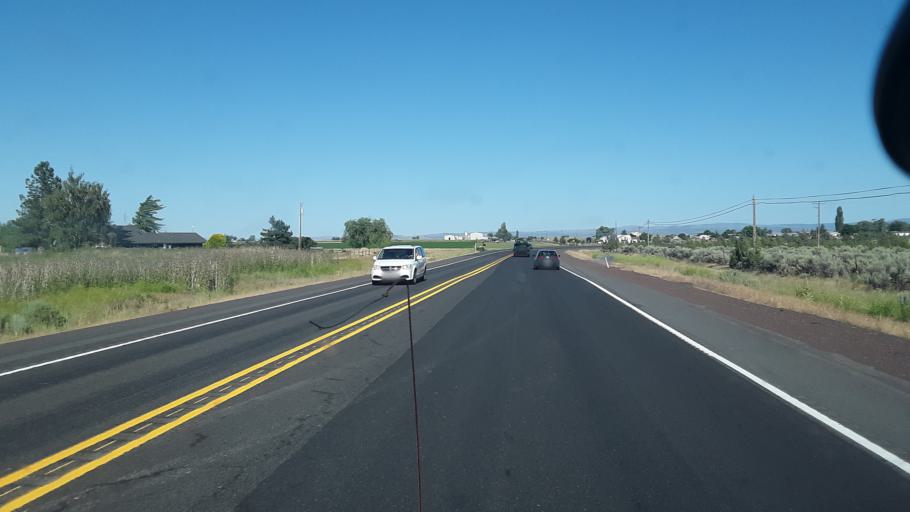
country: US
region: Oregon
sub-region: Jefferson County
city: Warm Springs
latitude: 44.7223
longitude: -121.1837
